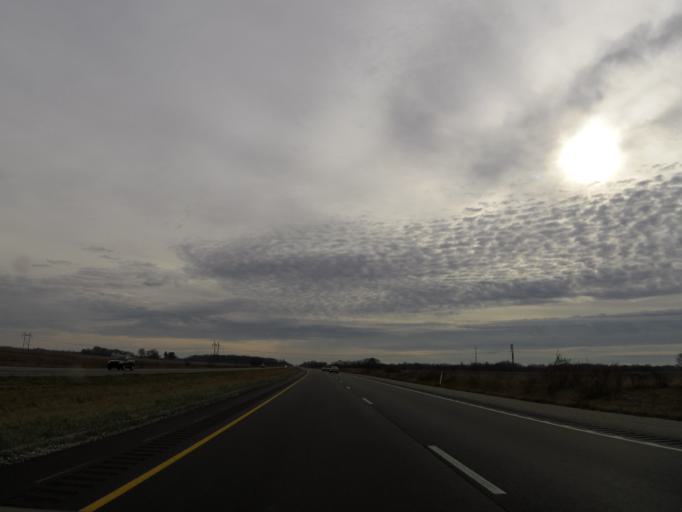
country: US
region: Indiana
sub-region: Montgomery County
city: Crawfordsville
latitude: 40.0077
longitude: -86.7524
